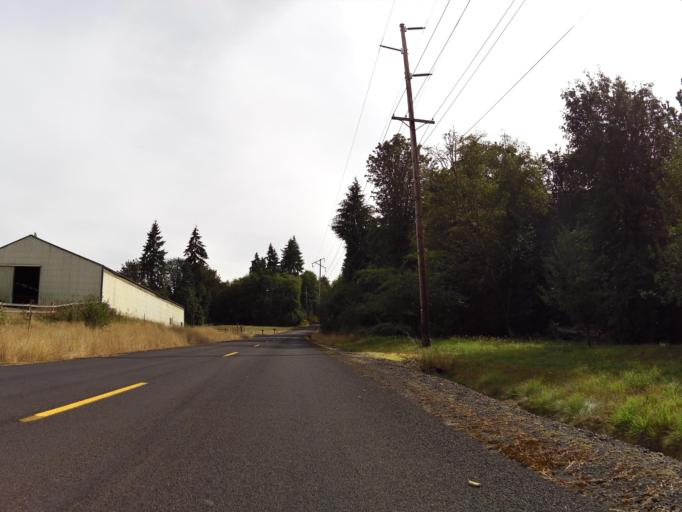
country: US
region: Washington
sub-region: Cowlitz County
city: Castle Rock
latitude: 46.3195
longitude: -122.9255
